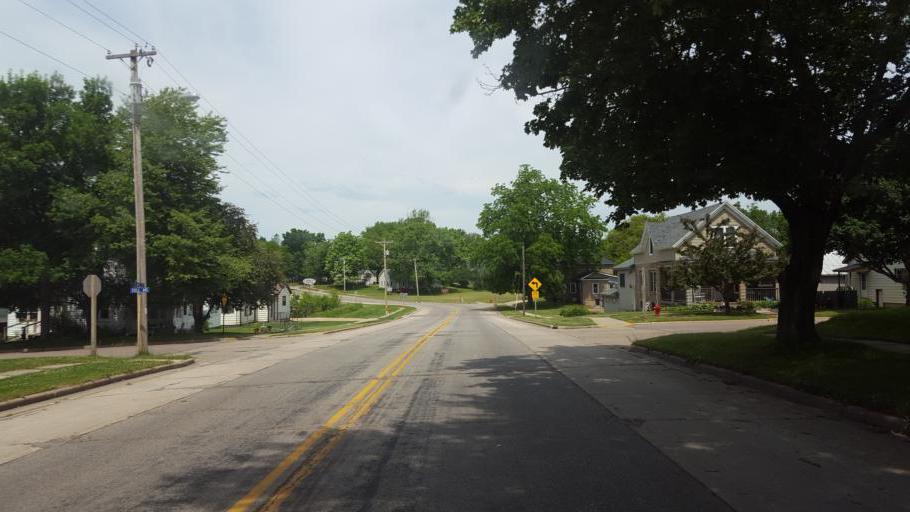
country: US
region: Wisconsin
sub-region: Vernon County
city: Hillsboro
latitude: 43.6513
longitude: -90.3453
